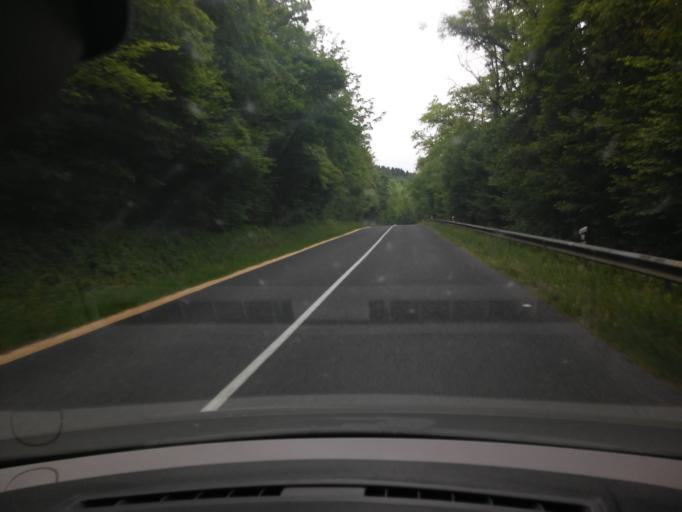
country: FR
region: Lorraine
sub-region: Departement de la Meuse
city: Lerouville
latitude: 48.8354
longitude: 5.5080
